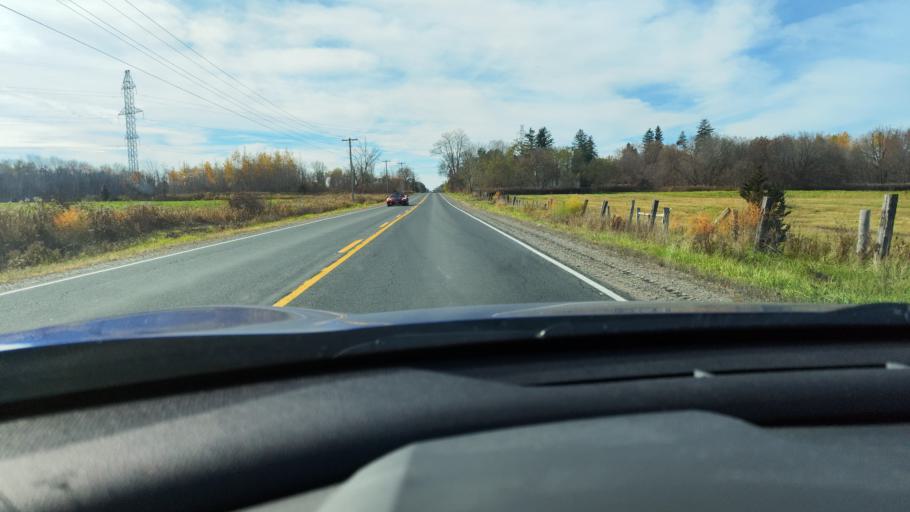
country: CA
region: Ontario
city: Angus
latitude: 44.3637
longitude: -79.9476
